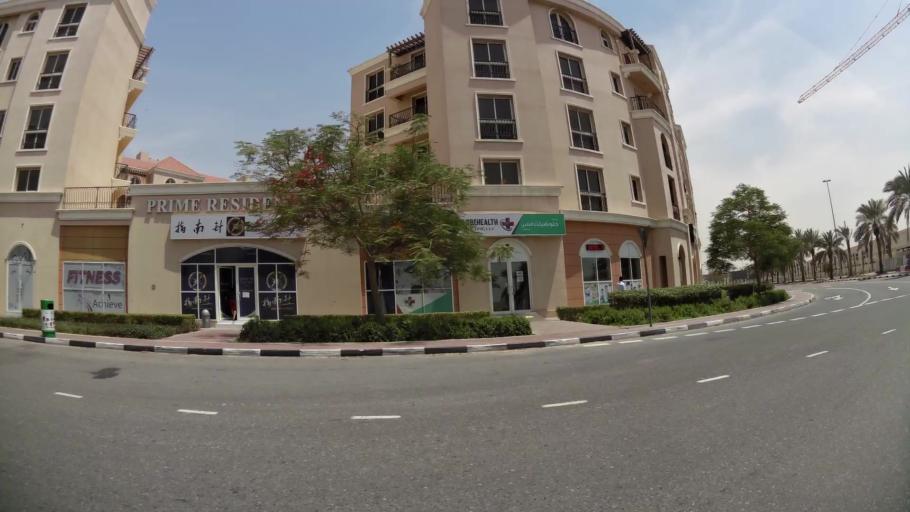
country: AE
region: Ash Shariqah
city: Sharjah
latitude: 25.1653
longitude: 55.3973
